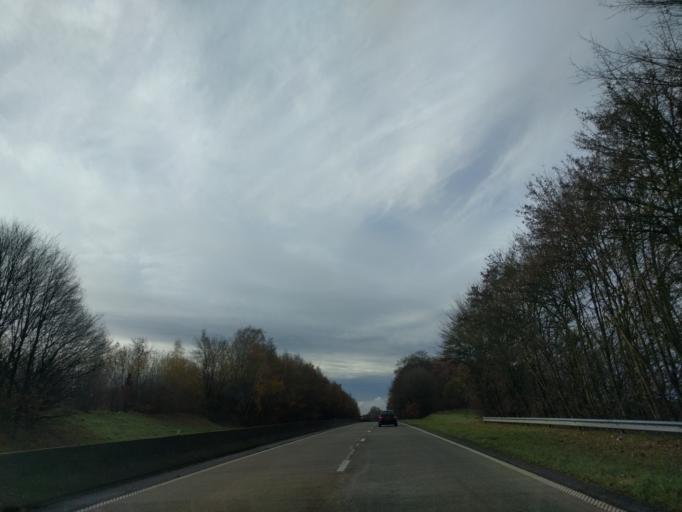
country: BE
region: Wallonia
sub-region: Province de Namur
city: Houyet
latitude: 50.2525
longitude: 5.0166
